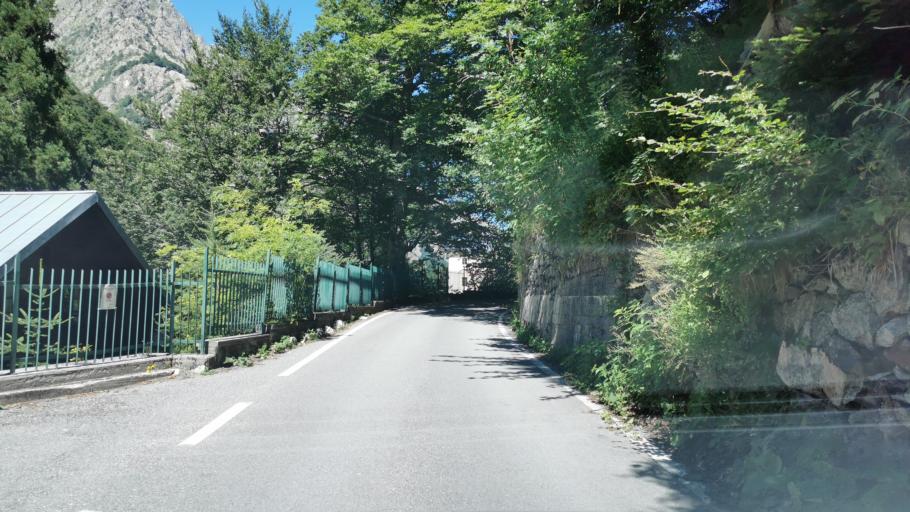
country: IT
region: Piedmont
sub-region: Provincia di Cuneo
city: Demonte
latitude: 44.2060
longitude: 7.2712
